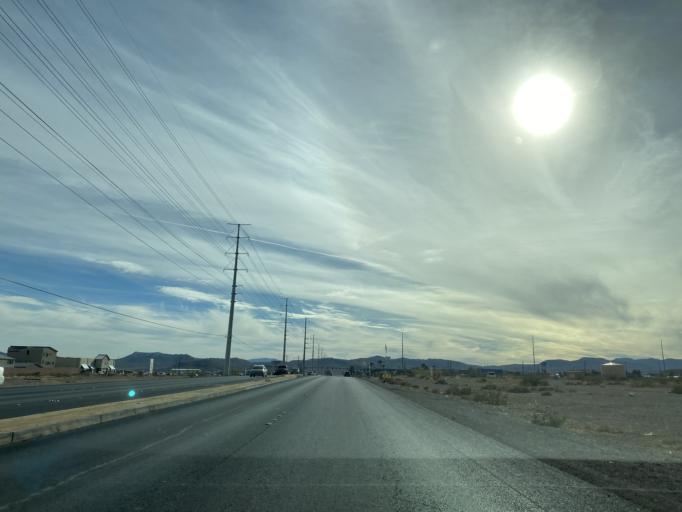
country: US
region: Nevada
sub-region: Clark County
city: Enterprise
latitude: 36.0266
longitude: -115.2435
